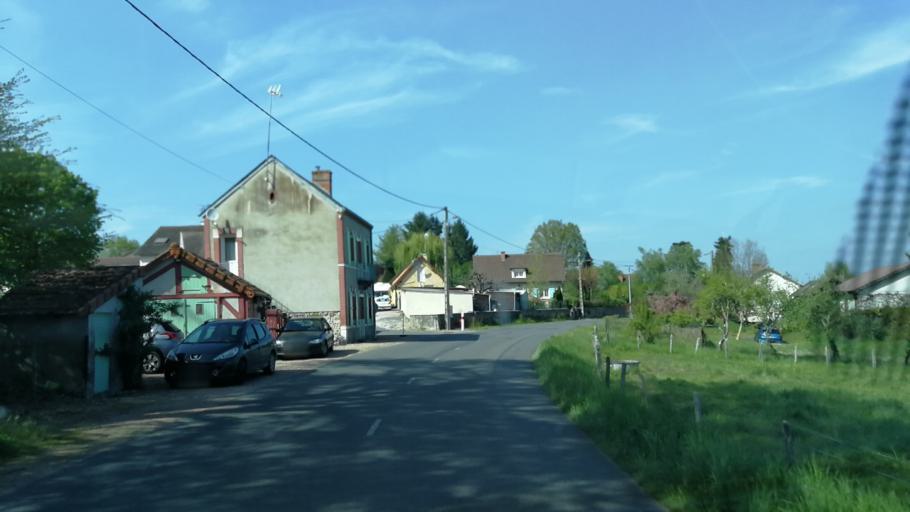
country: FR
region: Auvergne
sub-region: Departement de l'Allier
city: Saint-Gerand-le-Puy
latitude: 46.3820
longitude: 3.5829
